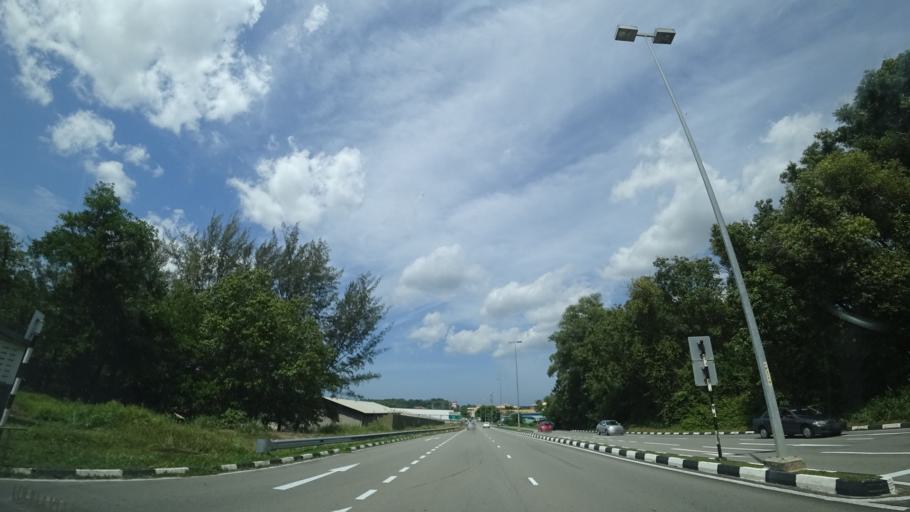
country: BN
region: Brunei and Muara
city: Bandar Seri Begawan
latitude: 4.9029
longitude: 114.9100
